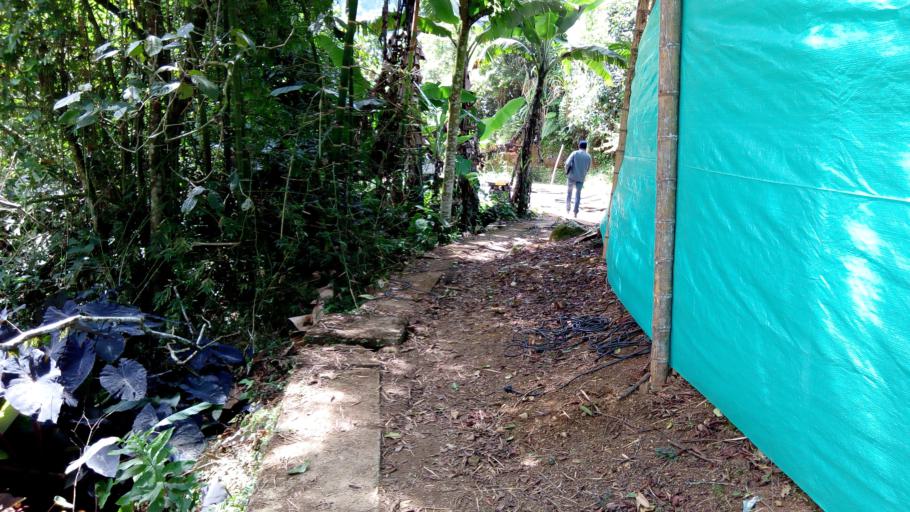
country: CO
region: Valle del Cauca
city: Jamundi
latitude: 3.3247
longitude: -76.6266
